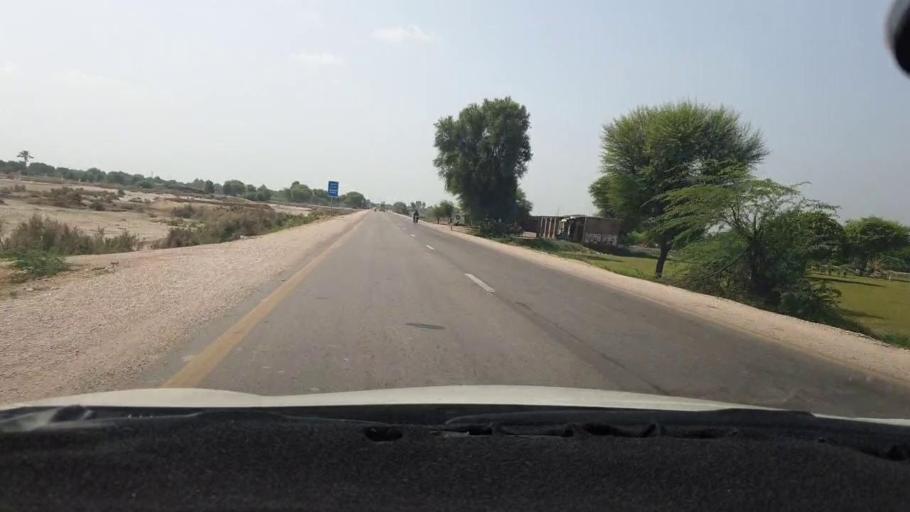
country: PK
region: Sindh
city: Mirpur Khas
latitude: 25.6320
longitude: 69.0925
